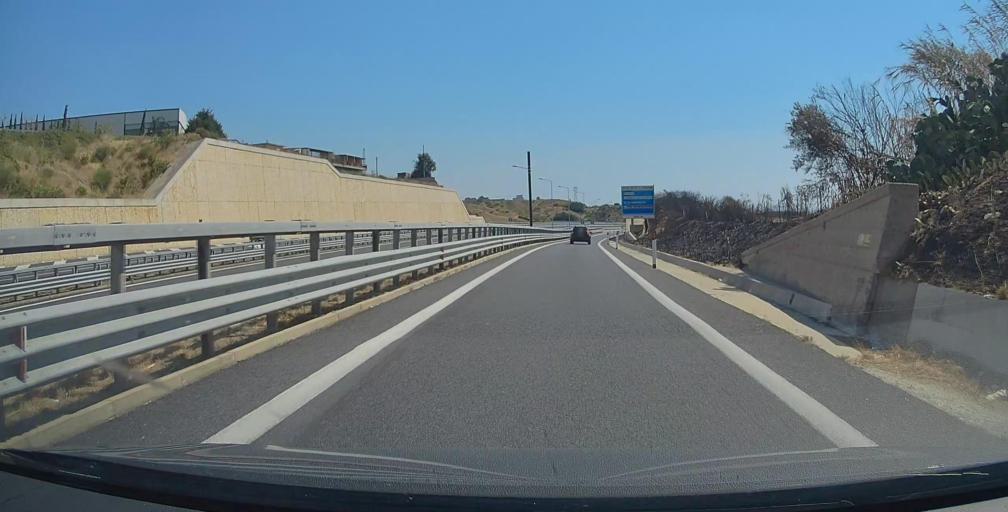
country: IT
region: Calabria
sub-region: Provincia di Reggio Calabria
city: Campo Calabro
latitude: 38.2157
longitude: 15.6475
